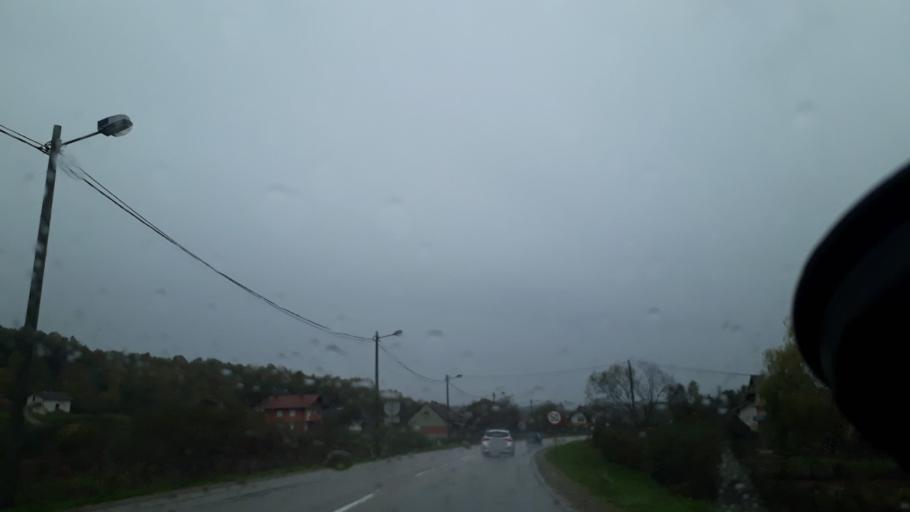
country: BA
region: Republika Srpska
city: Maglajani
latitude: 44.8574
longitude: 17.4392
